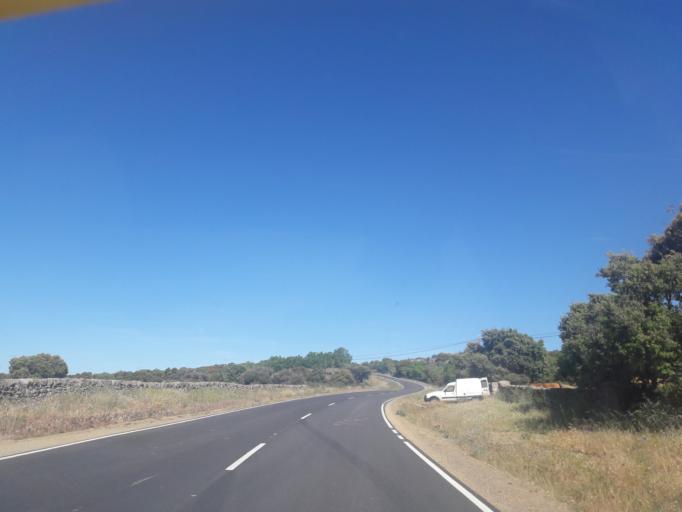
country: ES
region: Castille and Leon
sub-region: Provincia de Salamanca
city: Nava de Bejar
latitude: 40.4822
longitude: -5.6450
